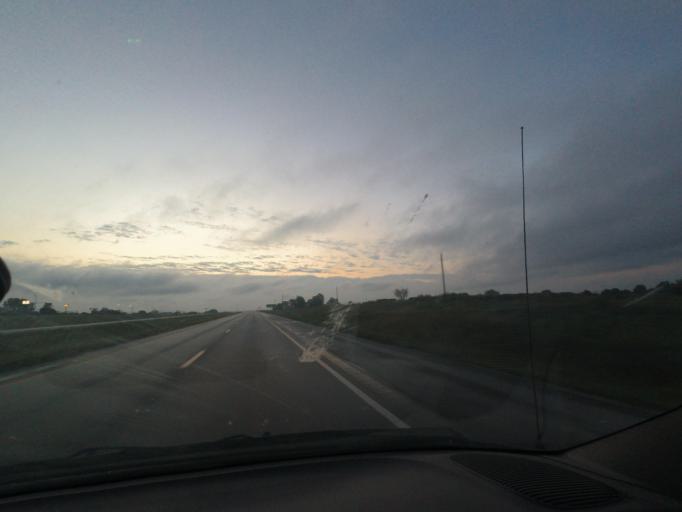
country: US
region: Missouri
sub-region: Linn County
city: Brookfield
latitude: 39.7624
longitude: -93.0124
